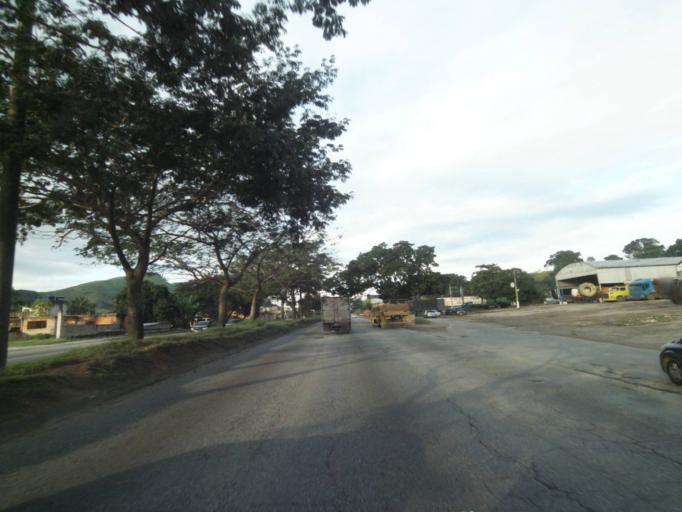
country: BR
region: Rio de Janeiro
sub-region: Nilopolis
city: Nilopolis
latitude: -22.8609
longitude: -43.5322
